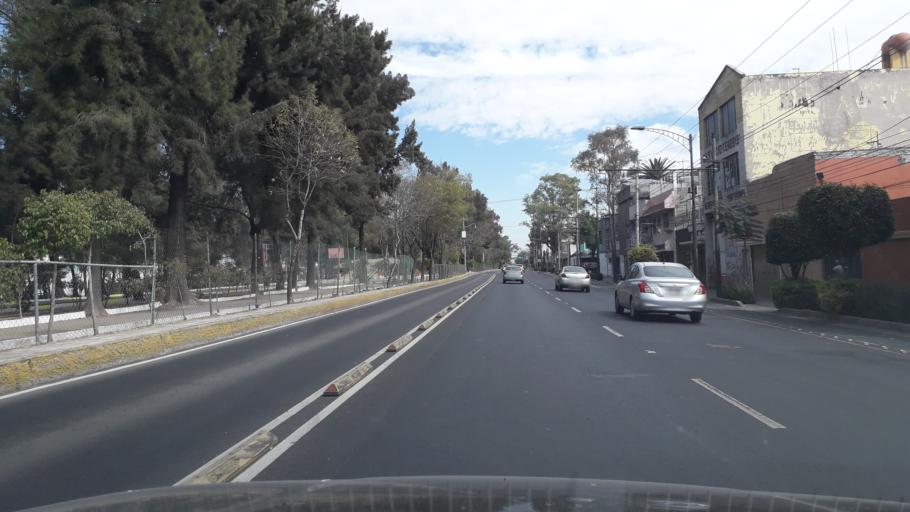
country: MX
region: Mexico City
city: Gustavo A. Madero
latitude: 19.4716
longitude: -99.1008
